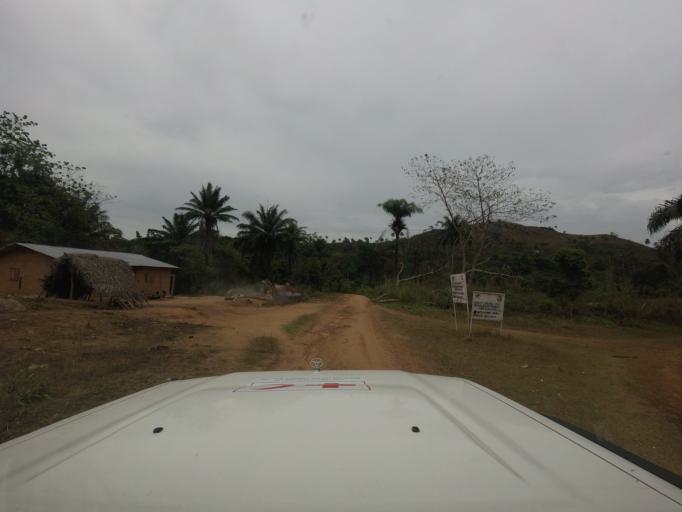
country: SL
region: Eastern Province
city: Buedu
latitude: 8.2743
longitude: -10.2772
